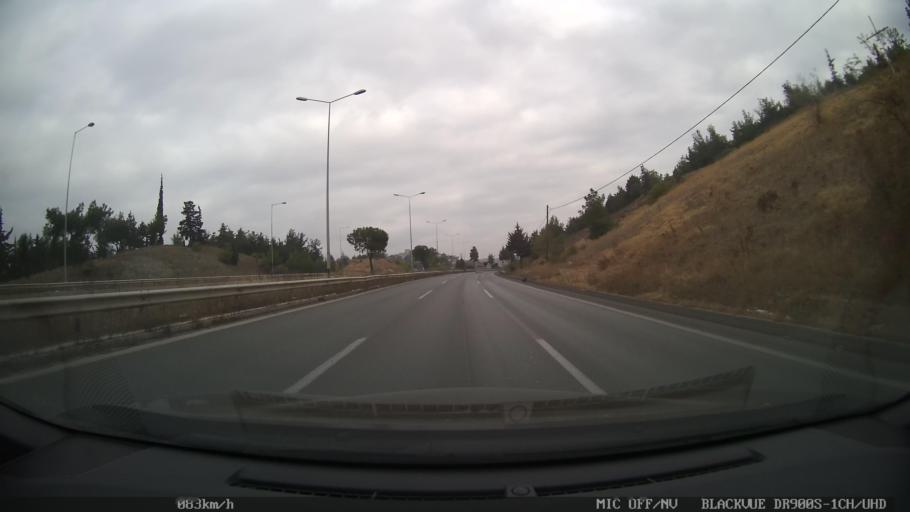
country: GR
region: Central Macedonia
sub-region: Nomos Thessalonikis
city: Agios Pavlos
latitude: 40.6532
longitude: 22.9664
